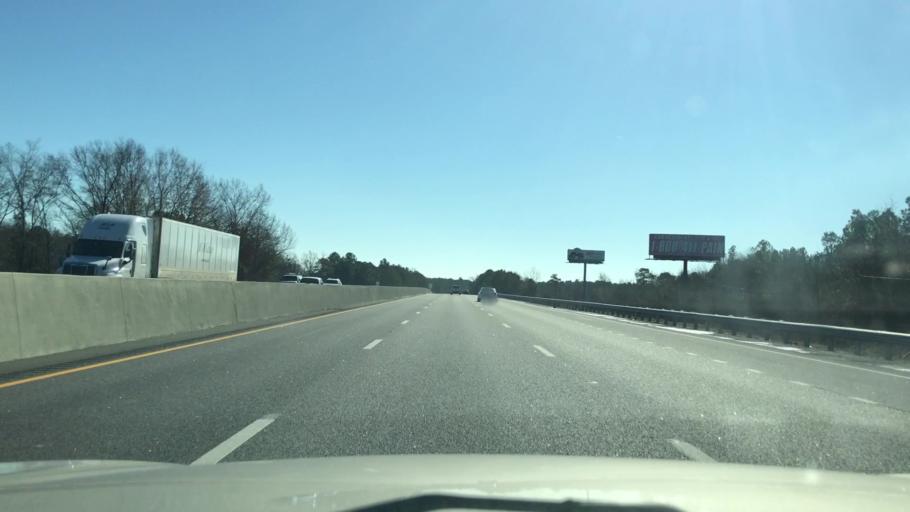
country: US
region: South Carolina
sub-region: Lexington County
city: Pineridge
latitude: 33.9178
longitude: -81.0637
